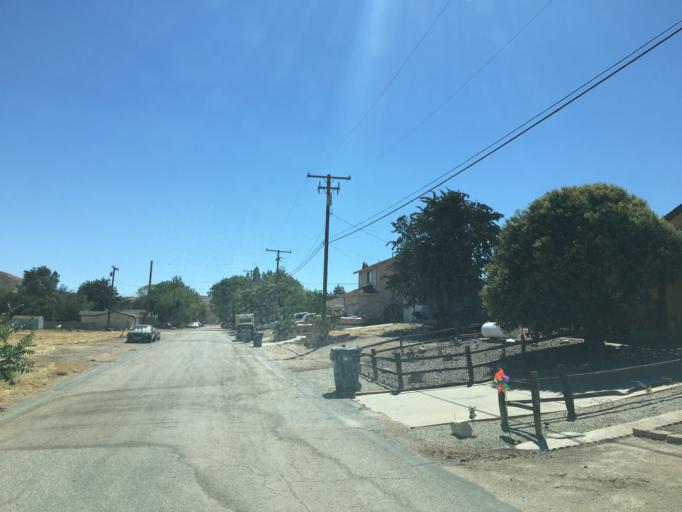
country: US
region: California
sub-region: Los Angeles County
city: Green Valley
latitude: 34.6577
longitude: -118.3808
